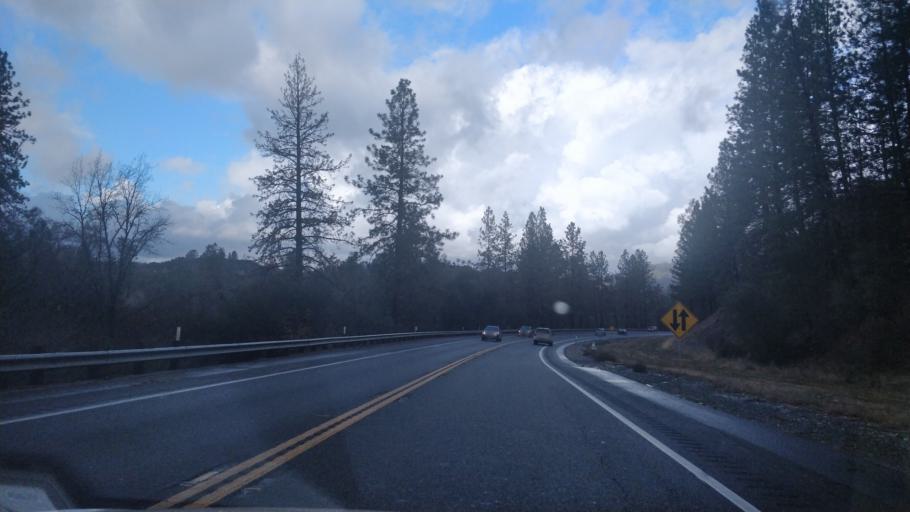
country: US
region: California
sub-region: Nevada County
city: Lake of the Pines
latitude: 39.0535
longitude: -121.0934
